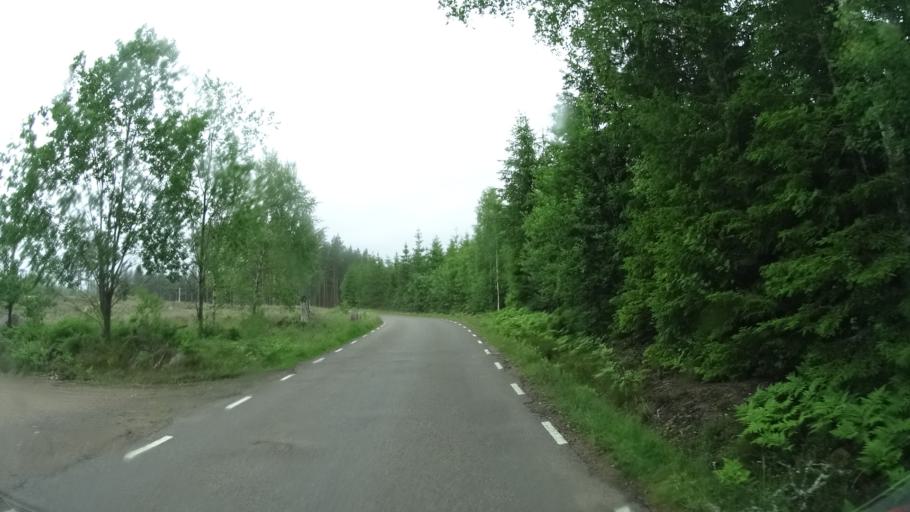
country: SE
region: Kalmar
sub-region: Vimmerby Kommun
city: Sodra Vi
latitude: 57.6971
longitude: 15.7298
